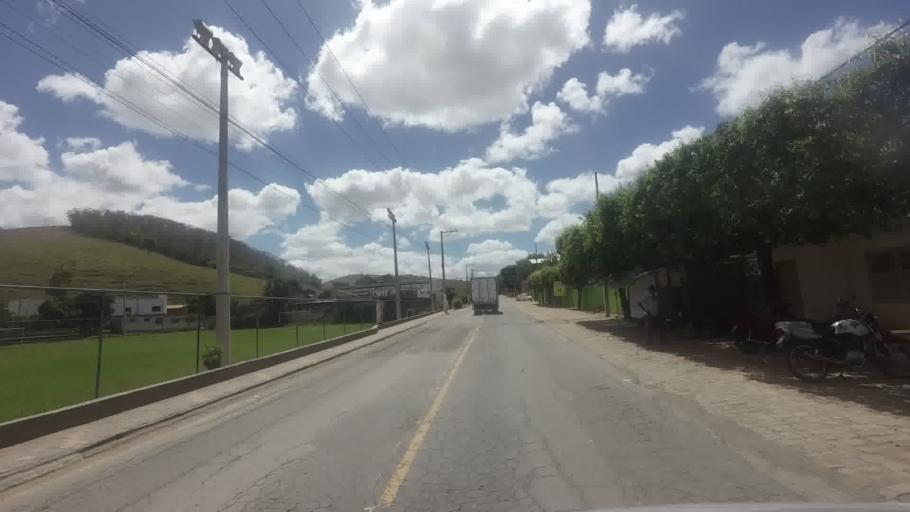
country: BR
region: Rio de Janeiro
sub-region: Santo Antonio De Padua
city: Santo Antonio de Padua
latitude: -21.6360
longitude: -42.2718
